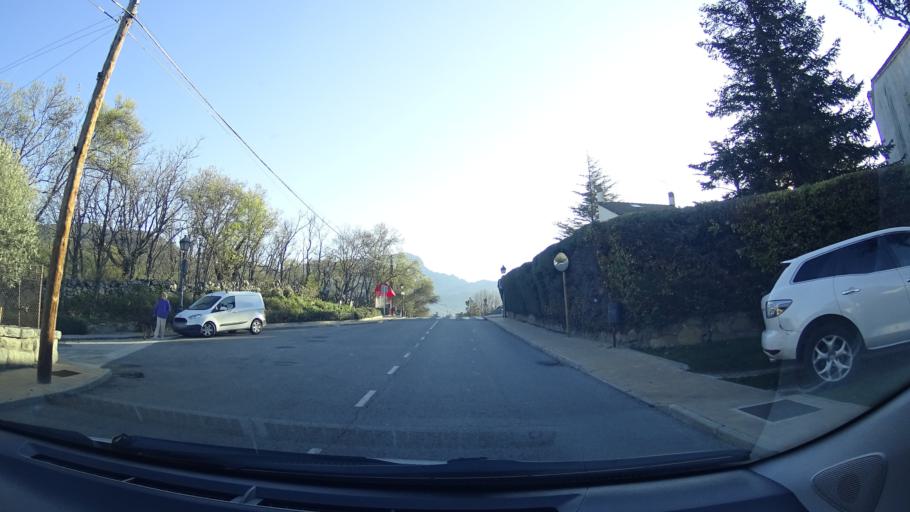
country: ES
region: Madrid
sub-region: Provincia de Madrid
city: Navacerrada
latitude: 40.7323
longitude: -4.0082
